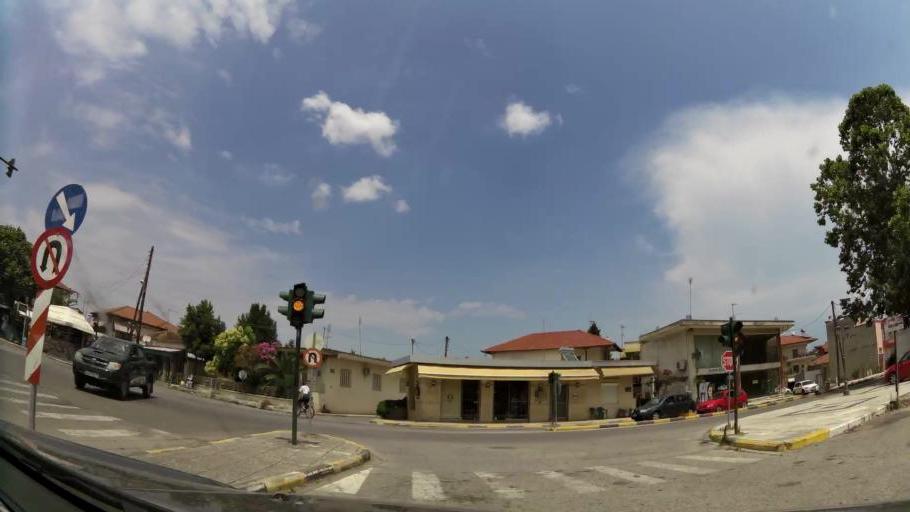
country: GR
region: Central Macedonia
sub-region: Nomos Pierias
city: Peristasi
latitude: 40.2741
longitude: 22.5420
